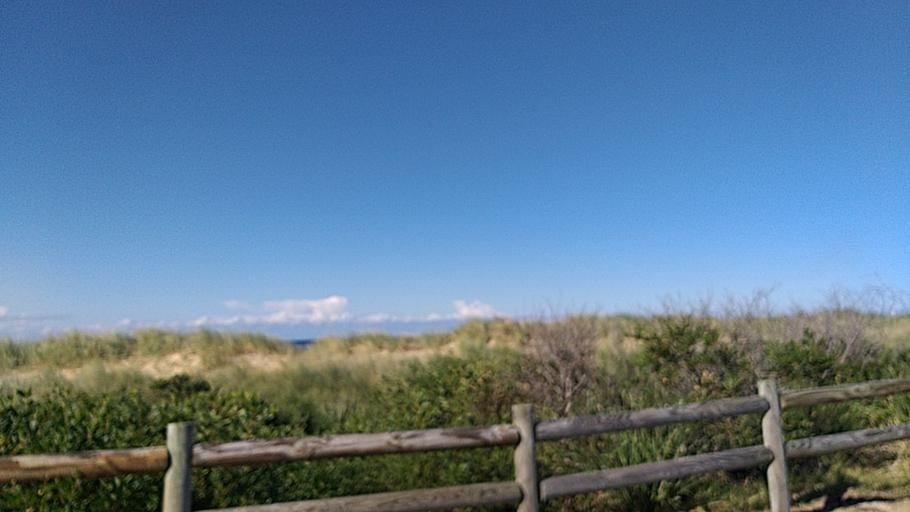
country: AU
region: New South Wales
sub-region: Wollongong
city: East Corrimal
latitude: -34.3869
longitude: 150.9121
